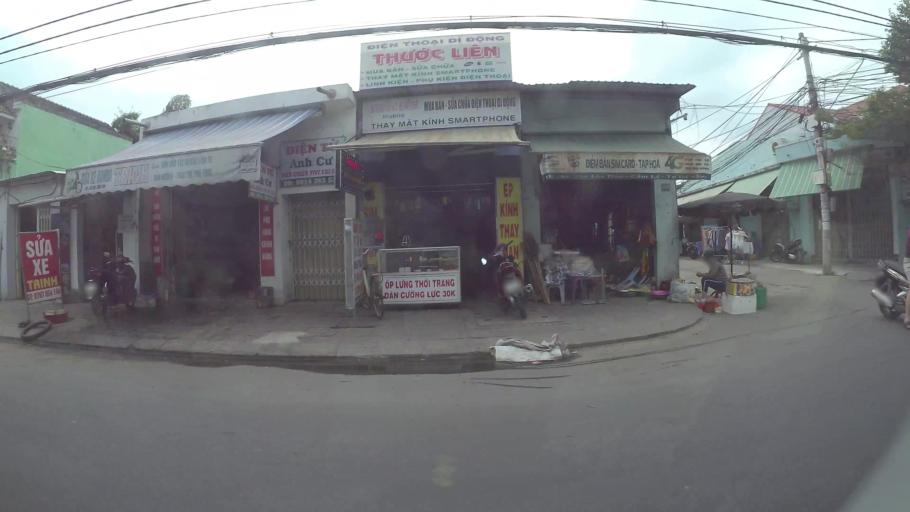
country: VN
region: Da Nang
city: Thanh Khe
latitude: 16.0480
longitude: 108.1814
